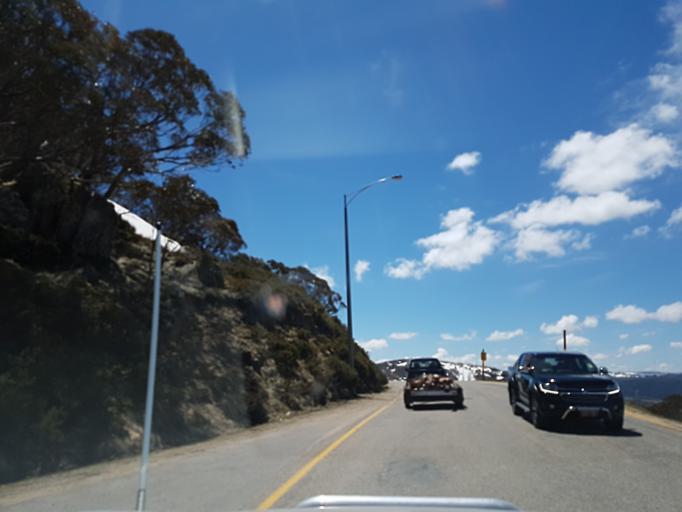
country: AU
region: Victoria
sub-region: Alpine
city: Mount Beauty
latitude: -36.9905
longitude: 147.1483
